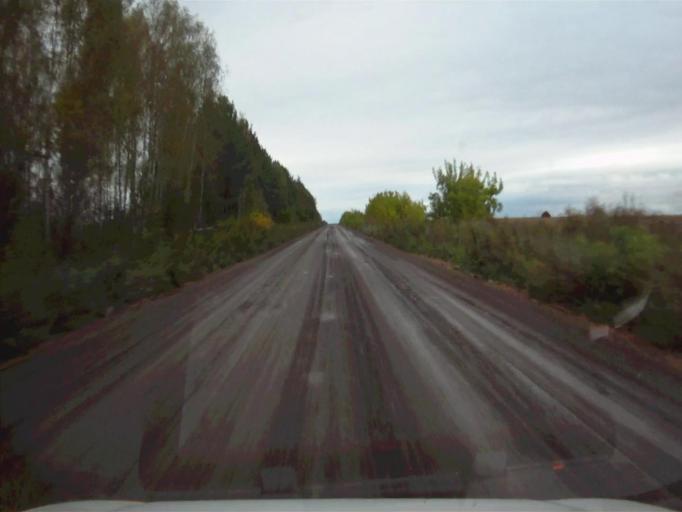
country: RU
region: Sverdlovsk
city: Mikhaylovsk
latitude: 56.1530
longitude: 59.2648
